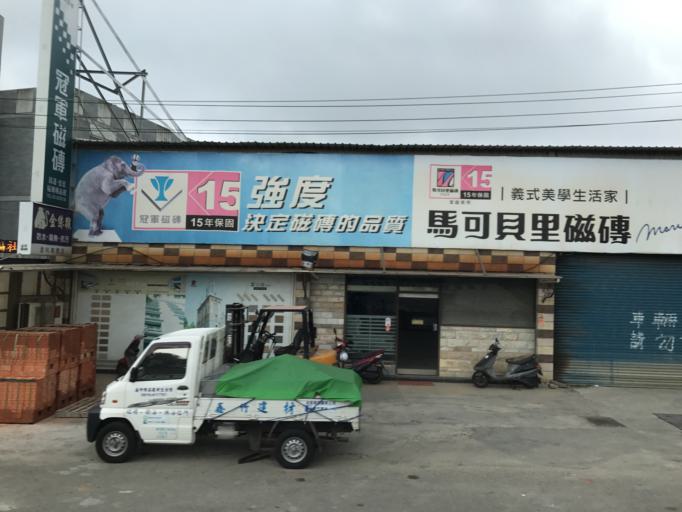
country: TW
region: Taiwan
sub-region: Hsinchu
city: Hsinchu
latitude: 24.8176
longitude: 120.9561
